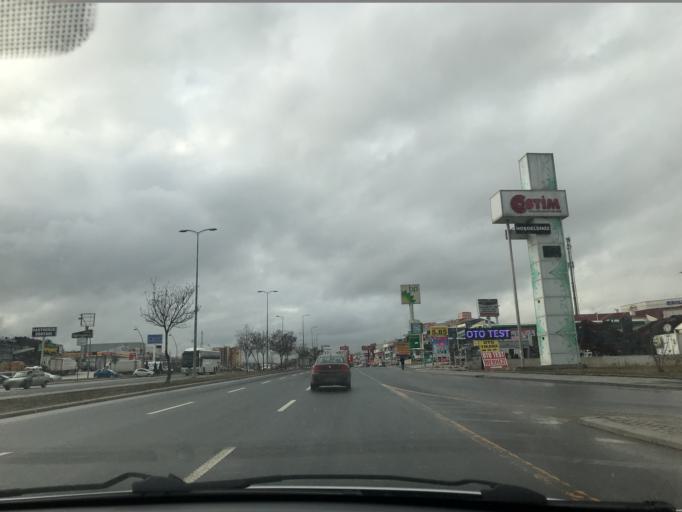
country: TR
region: Ankara
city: Batikent
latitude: 39.9636
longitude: 32.7561
